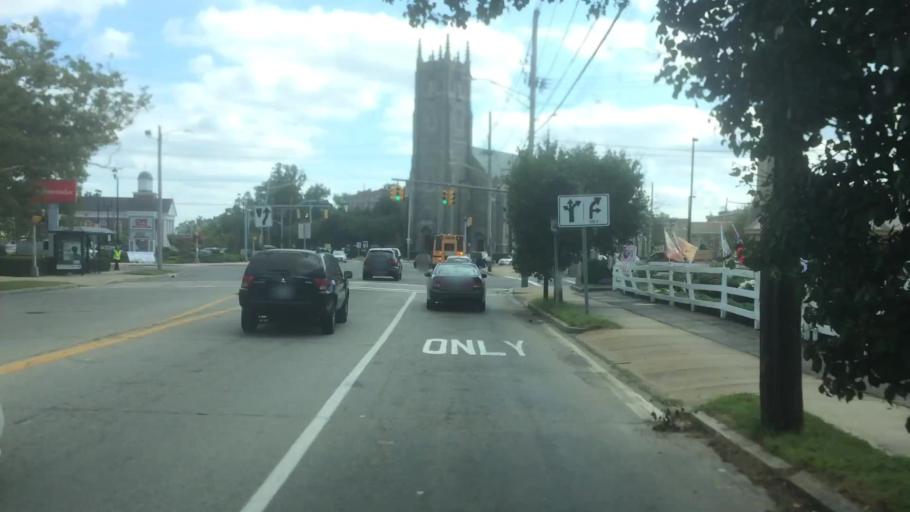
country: US
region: Rhode Island
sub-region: Providence County
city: Cranston
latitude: 41.7786
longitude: -71.4006
